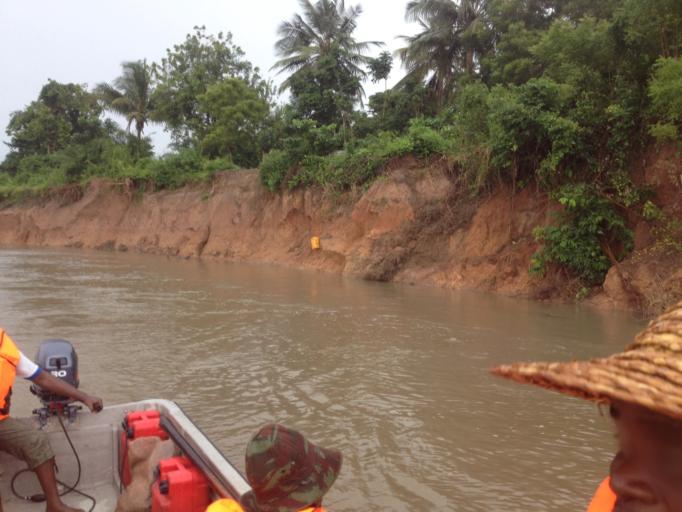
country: BJ
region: Mono
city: Lokossa
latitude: 6.5507
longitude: 1.6891
